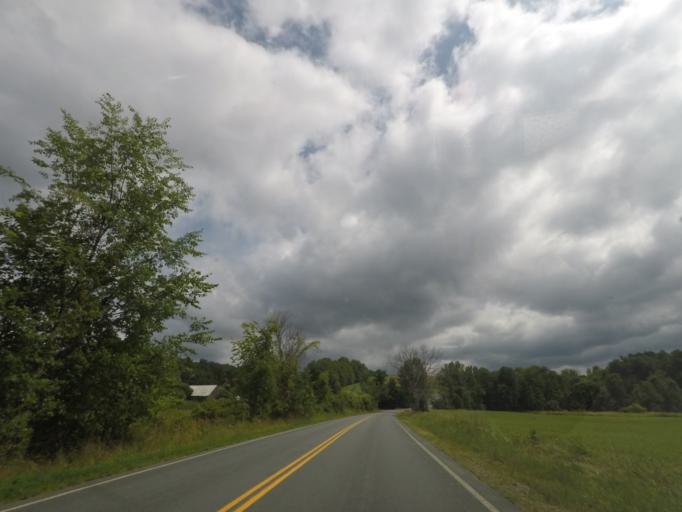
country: US
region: New York
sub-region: Saratoga County
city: Stillwater
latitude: 42.8888
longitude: -73.5610
